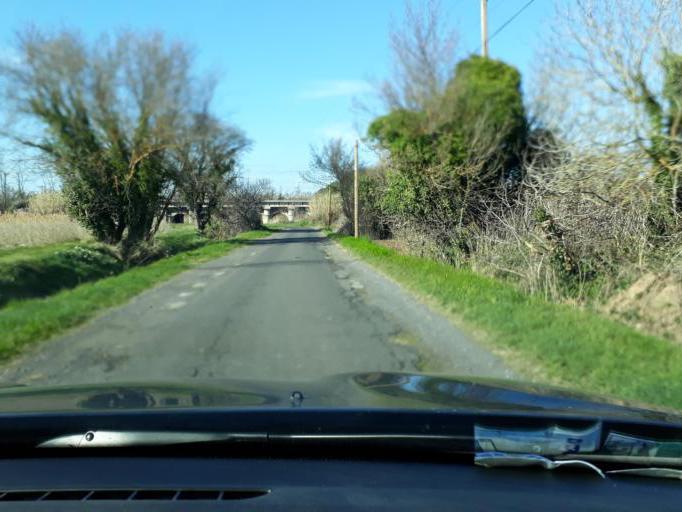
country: FR
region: Languedoc-Roussillon
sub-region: Departement de l'Herault
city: Agde
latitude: 43.3152
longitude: 3.4589
